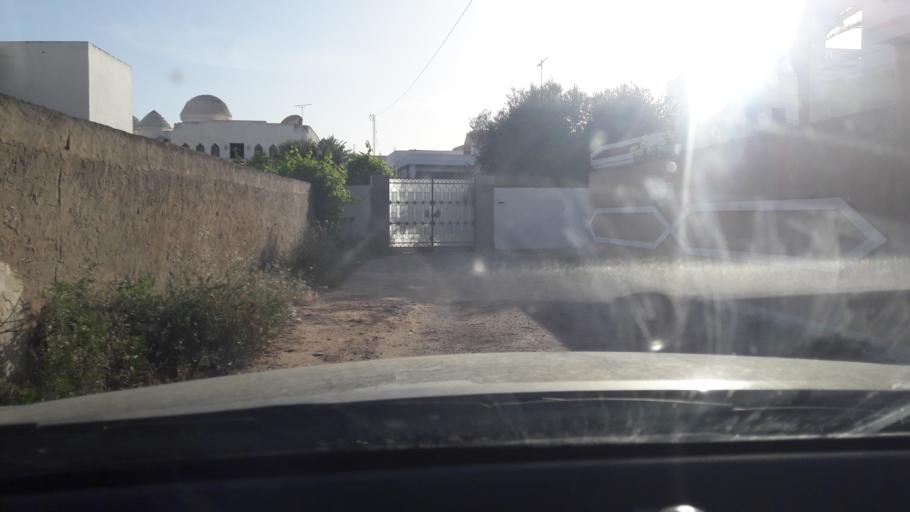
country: TN
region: Safaqis
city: Al Qarmadah
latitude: 34.7972
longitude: 10.7598
